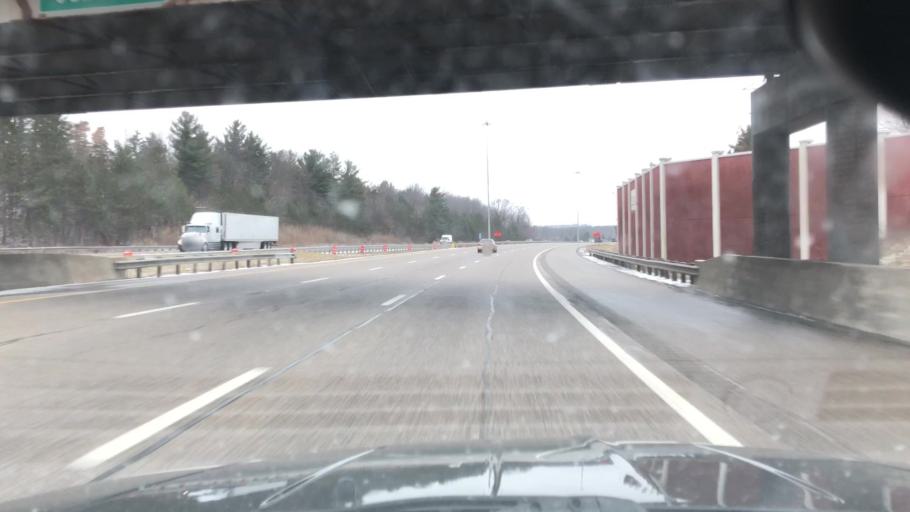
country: US
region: Ohio
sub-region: Cuyahoga County
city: Brecksville
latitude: 41.3077
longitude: -81.6482
